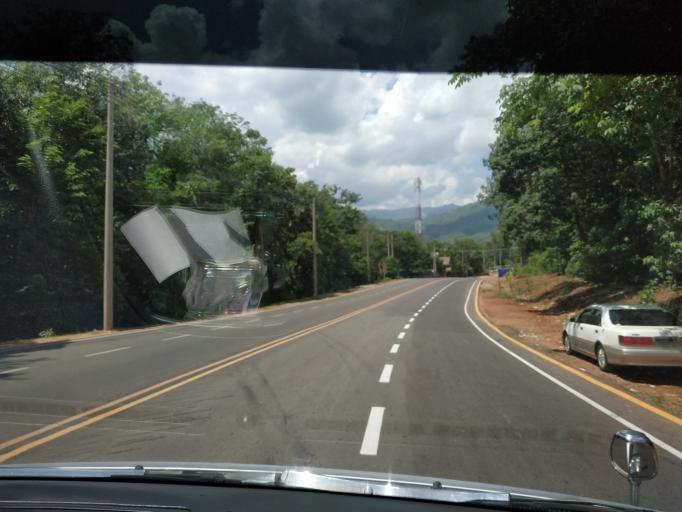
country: MM
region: Mon
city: Kyaikto
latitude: 17.3945
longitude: 97.0730
